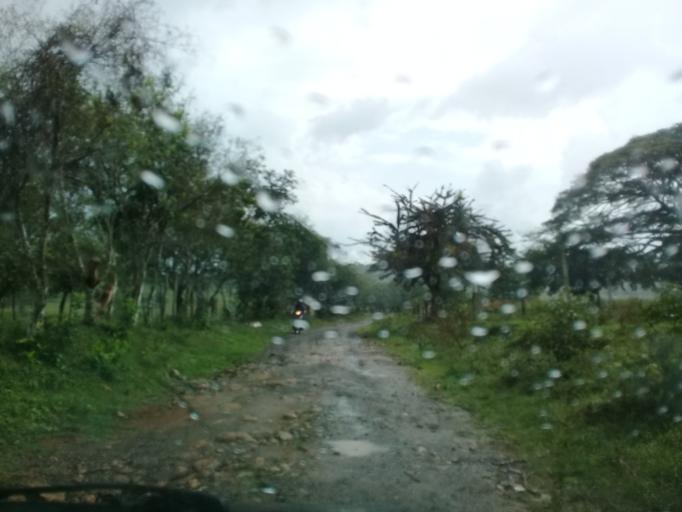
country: CO
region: Cundinamarca
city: Guaduas
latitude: 5.1008
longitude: -74.6062
